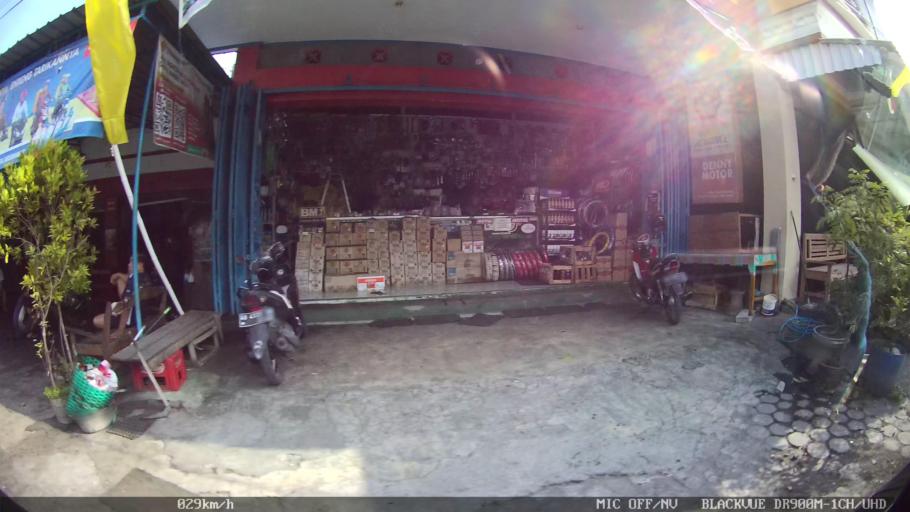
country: ID
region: Daerah Istimewa Yogyakarta
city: Kasihan
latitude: -7.8285
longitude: 110.3313
